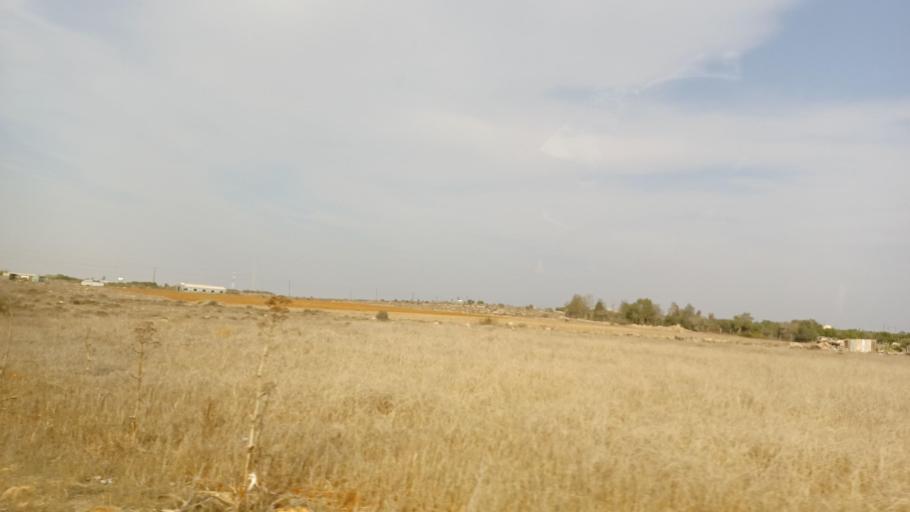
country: CY
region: Ammochostos
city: Frenaros
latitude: 35.0577
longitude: 33.8988
